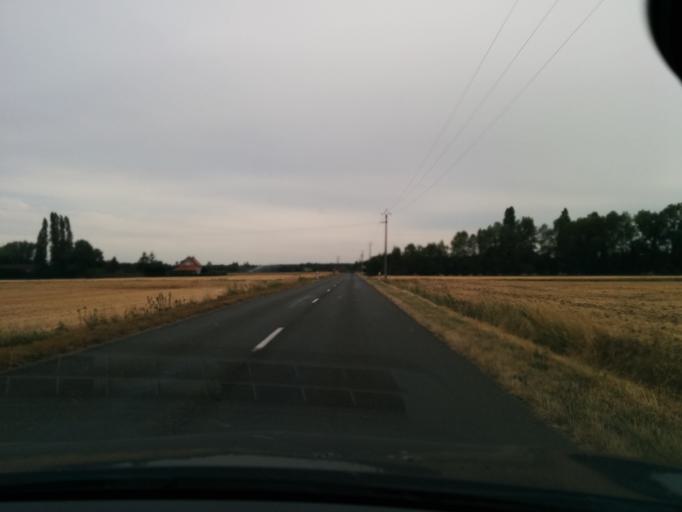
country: FR
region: Centre
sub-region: Departement du Loiret
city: Tigy
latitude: 47.8103
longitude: 2.2064
